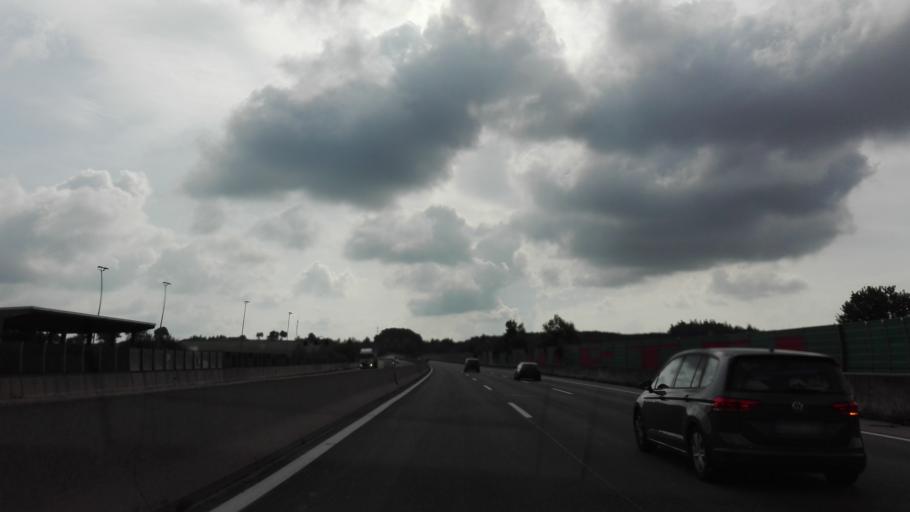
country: AT
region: Lower Austria
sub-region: Politischer Bezirk Amstetten
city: Wolfsbach
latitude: 48.1121
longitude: 14.6779
